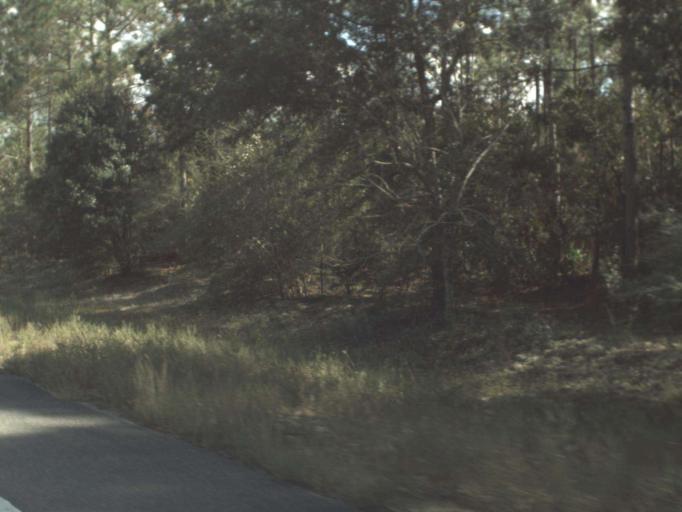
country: US
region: Florida
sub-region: Bay County
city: Laguna Beach
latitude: 30.4446
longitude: -85.8296
